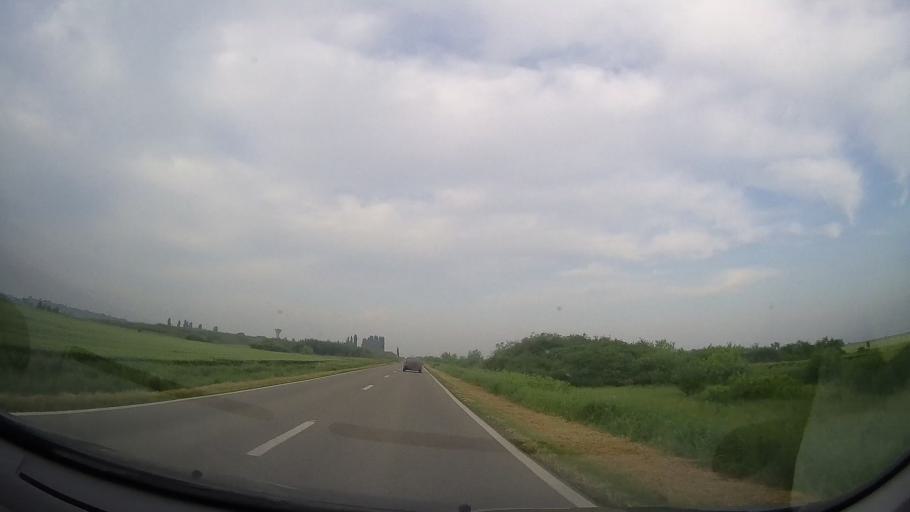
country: RO
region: Timis
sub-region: Comuna Parta
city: Parta
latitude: 45.6359
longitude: 21.1105
